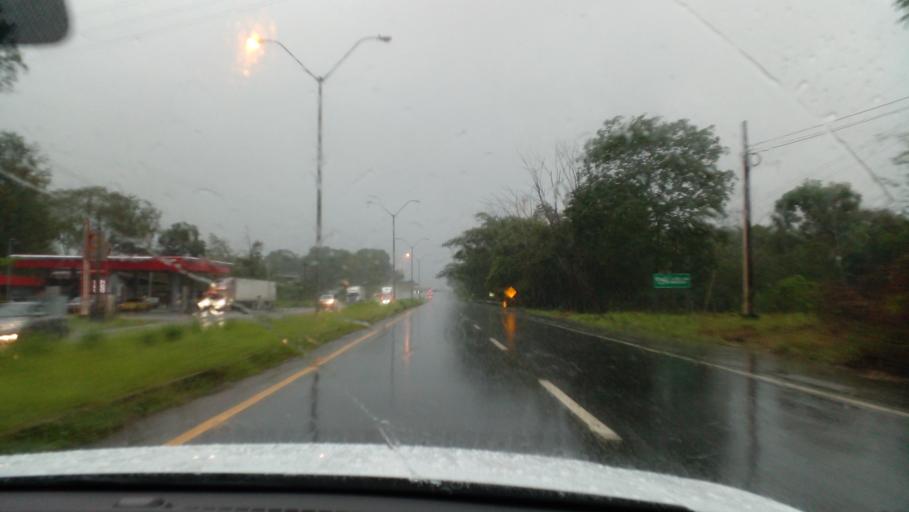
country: PA
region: Chiriqui
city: San Felix
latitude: 8.2777
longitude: -81.8770
